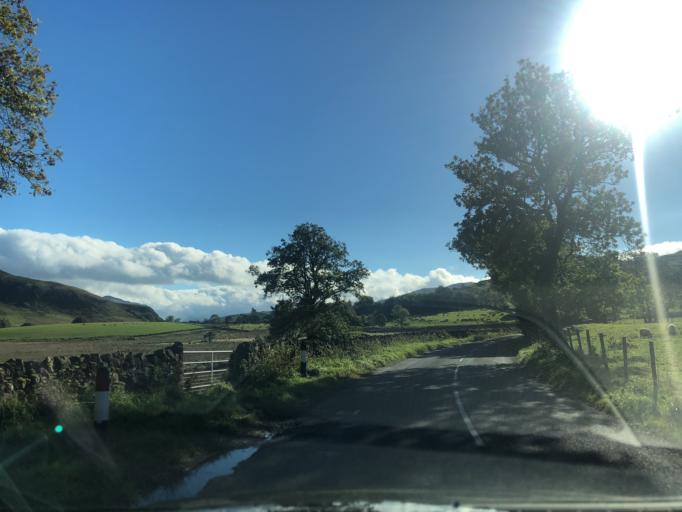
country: GB
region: England
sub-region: Cumbria
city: Ambleside
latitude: 54.6004
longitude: -2.9353
